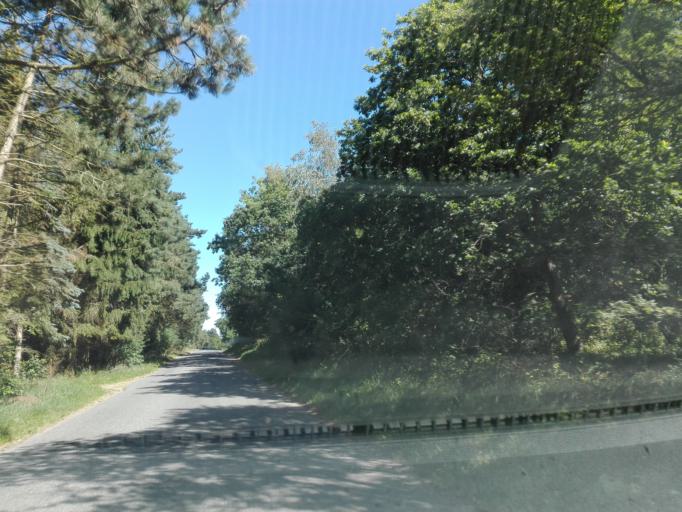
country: DK
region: Central Jutland
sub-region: Arhus Kommune
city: Malling
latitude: 55.9970
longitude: 10.2482
